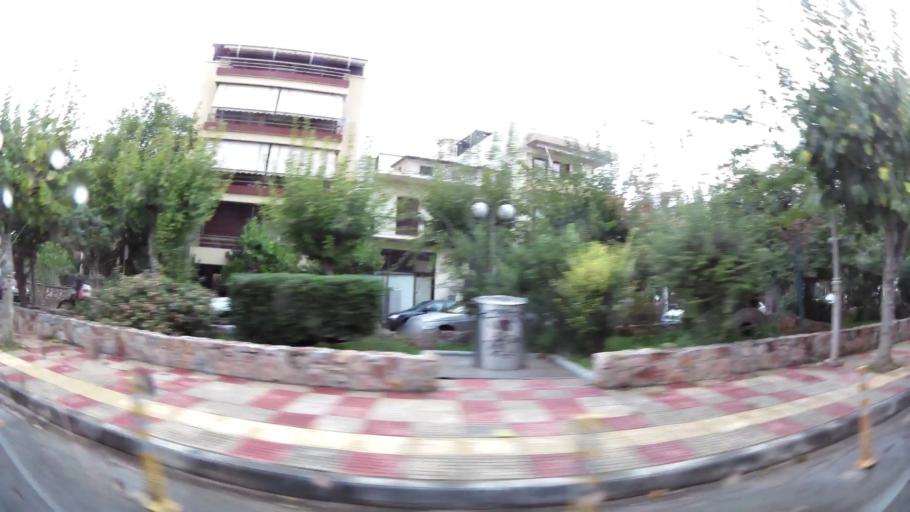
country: GR
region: Attica
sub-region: Nomarchia Athinas
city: Ymittos
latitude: 37.9553
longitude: 23.7424
